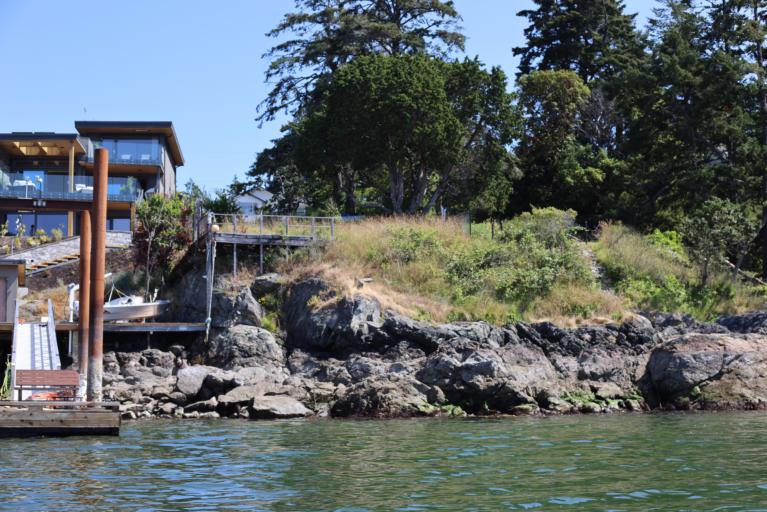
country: CA
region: British Columbia
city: Colwood
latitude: 48.4510
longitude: -123.4418
